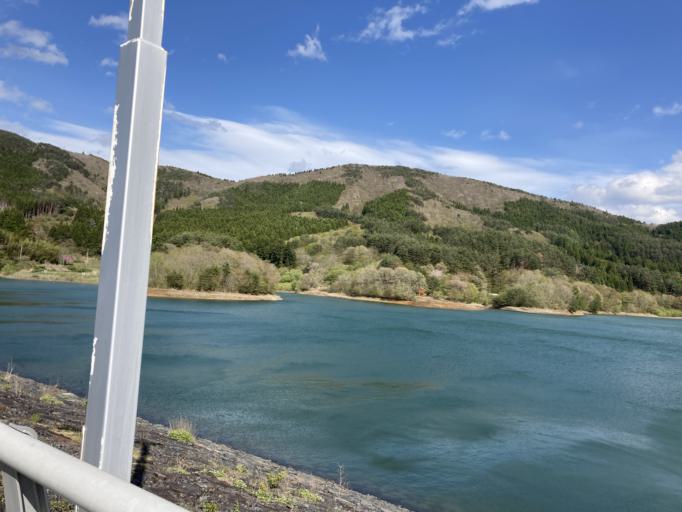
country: JP
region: Iwate
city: Ichinoseki
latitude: 38.8427
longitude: 141.3934
